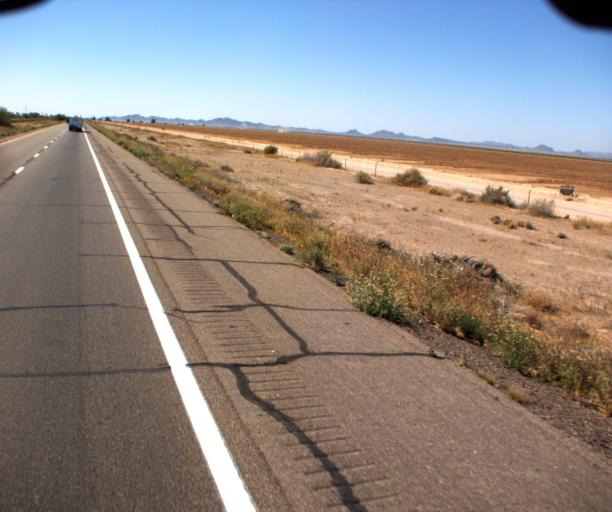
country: US
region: Arizona
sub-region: Maricopa County
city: Gila Bend
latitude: 32.9258
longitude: -112.8590
